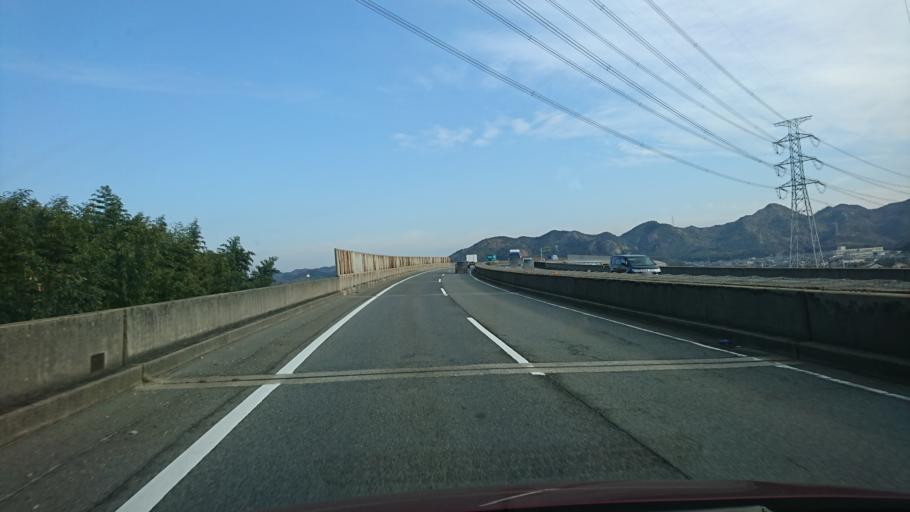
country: JP
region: Hyogo
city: Shirahamacho-usazakiminami
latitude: 34.8081
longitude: 134.7430
